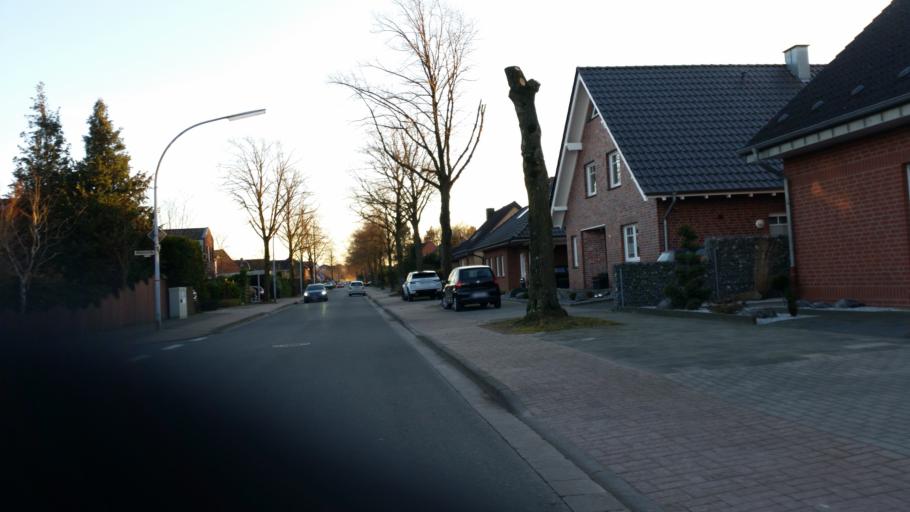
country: DE
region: North Rhine-Westphalia
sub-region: Regierungsbezirk Munster
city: Rheine
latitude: 52.2825
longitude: 7.4078
